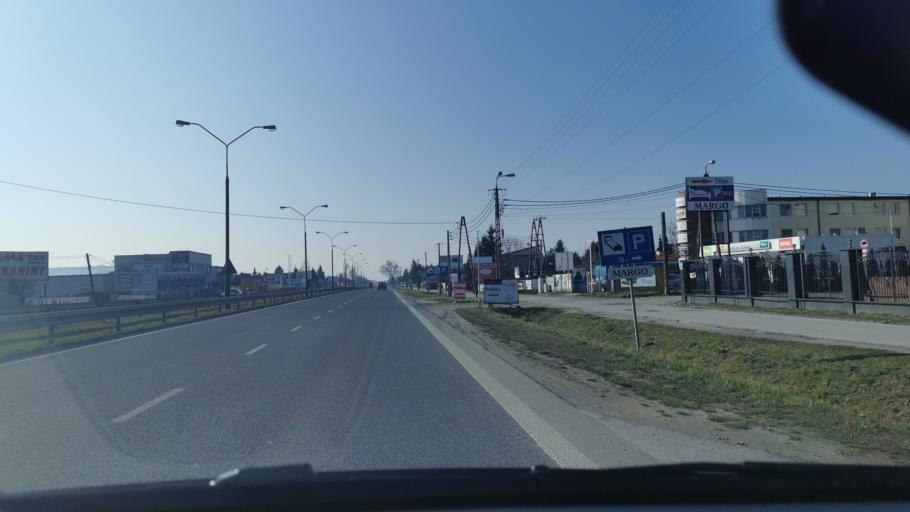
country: PL
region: Masovian Voivodeship
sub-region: Powiat pruszkowski
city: Nowe Grocholice
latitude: 52.1281
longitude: 20.8962
